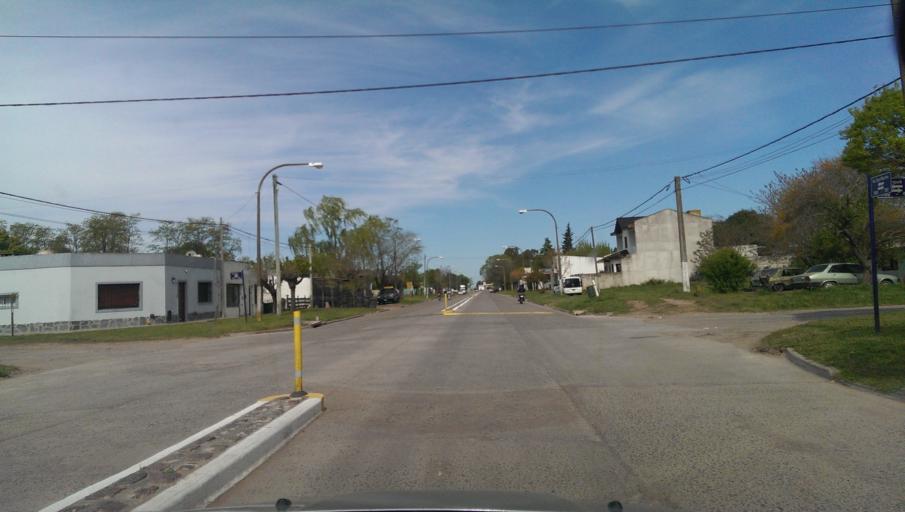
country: AR
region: Buenos Aires
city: Tapalque
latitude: -36.3841
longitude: -59.4972
